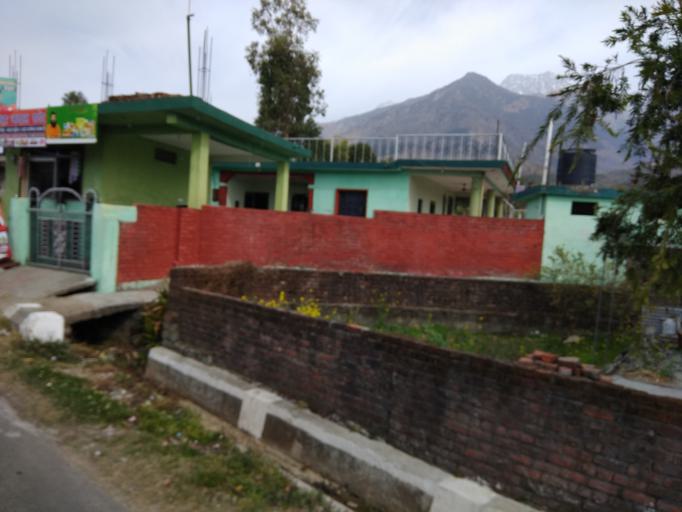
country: IN
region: Himachal Pradesh
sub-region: Kangra
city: Dharmsala
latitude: 32.1588
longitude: 76.4110
